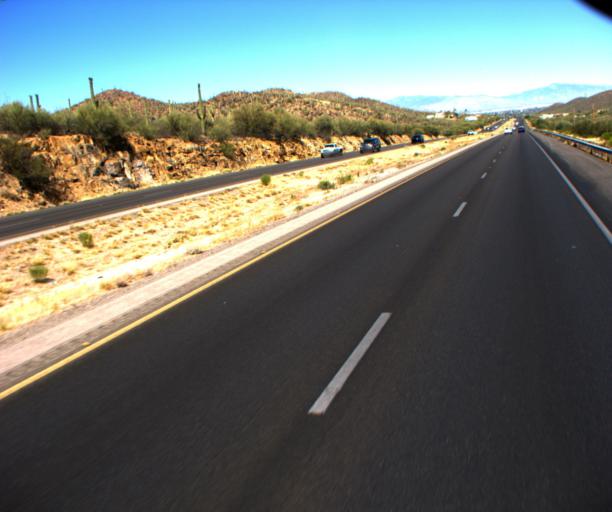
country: US
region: Arizona
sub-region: Pima County
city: Drexel Heights
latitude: 32.1772
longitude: -111.0378
